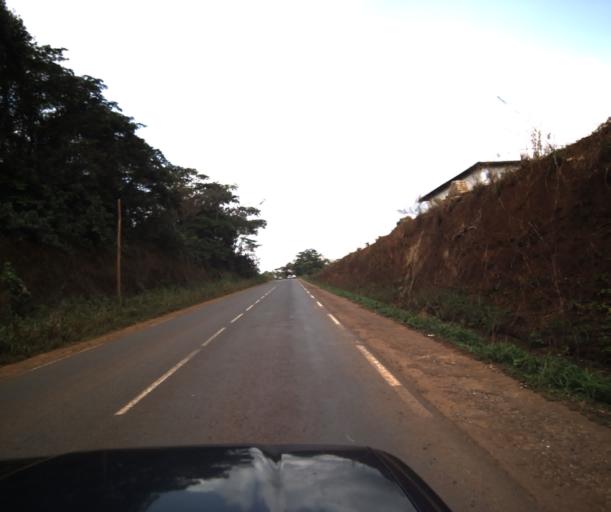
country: CM
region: Centre
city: Mbankomo
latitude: 3.7914
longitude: 11.4136
